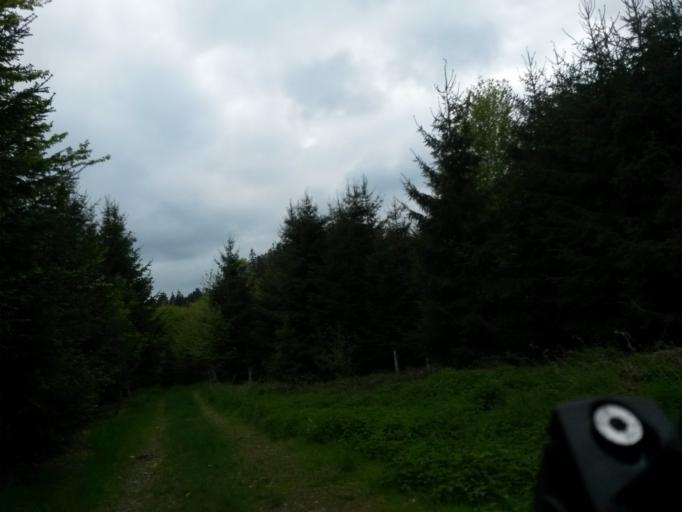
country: DE
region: Baden-Wuerttemberg
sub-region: Tuebingen Region
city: Bad Waldsee
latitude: 47.9367
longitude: 9.7910
